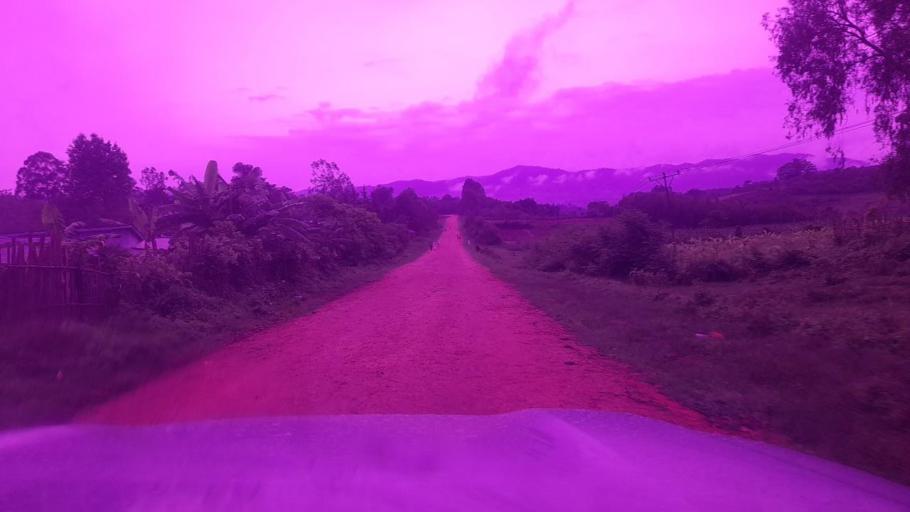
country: ET
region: Southern Nations, Nationalities, and People's Region
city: Bonga
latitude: 7.4401
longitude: 36.1606
